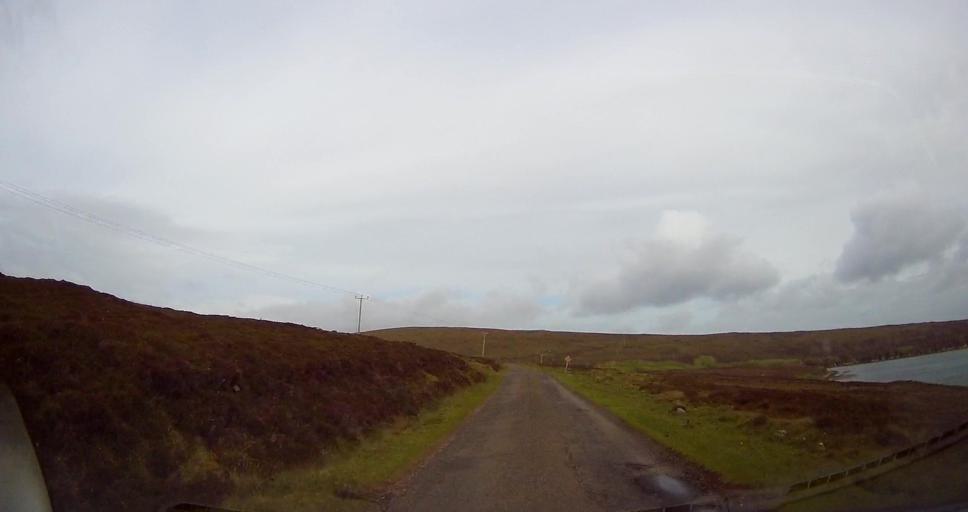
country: GB
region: Scotland
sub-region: Orkney Islands
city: Stromness
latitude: 58.8570
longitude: -3.2143
